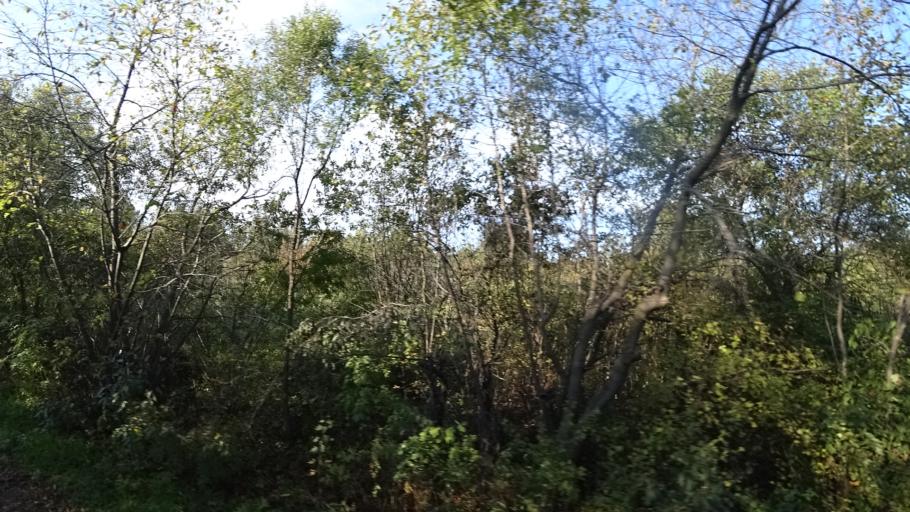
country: RU
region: Amur
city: Arkhara
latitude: 49.3499
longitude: 130.1162
